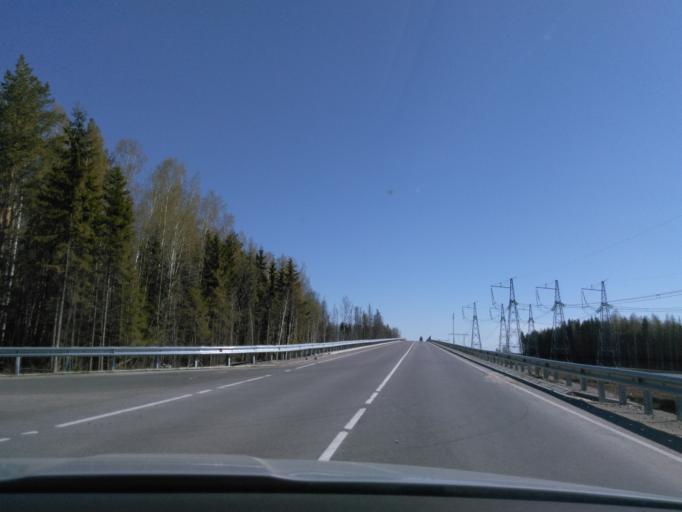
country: RU
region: Moskovskaya
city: Mendeleyevo
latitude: 56.0614
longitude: 37.2334
